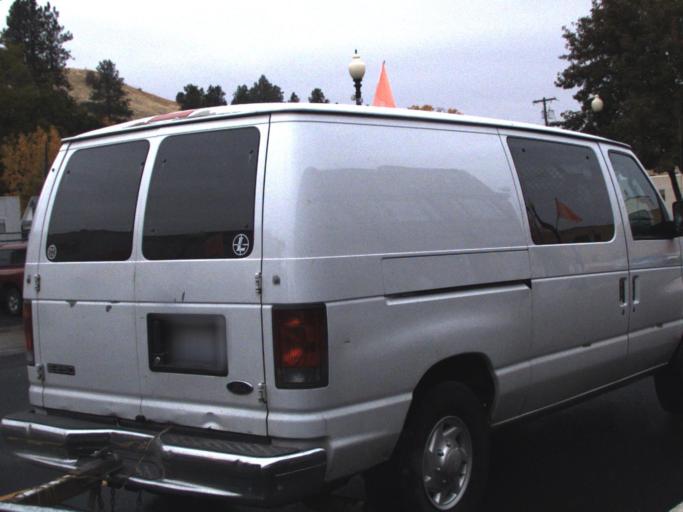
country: US
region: Washington
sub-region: Whitman County
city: Colfax
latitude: 46.8833
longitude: -117.3646
